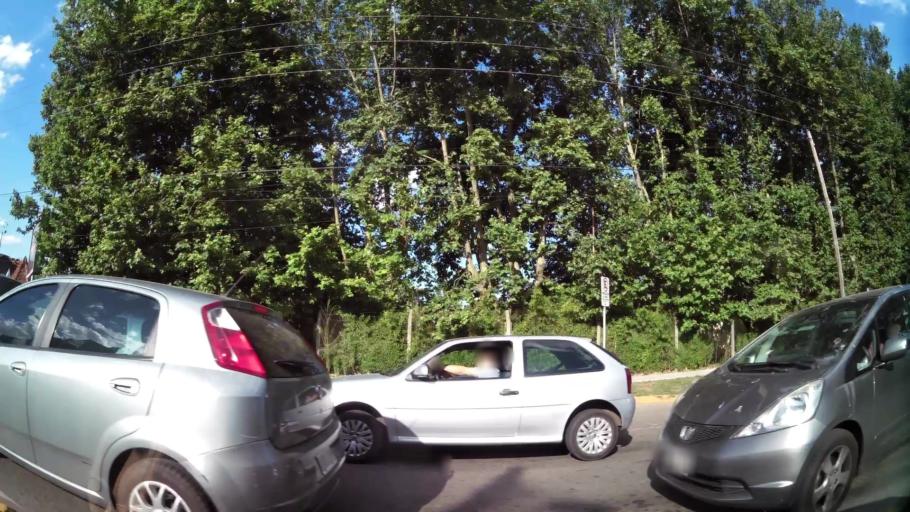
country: AR
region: Buenos Aires
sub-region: Partido de San Isidro
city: San Isidro
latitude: -34.4926
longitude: -58.5468
